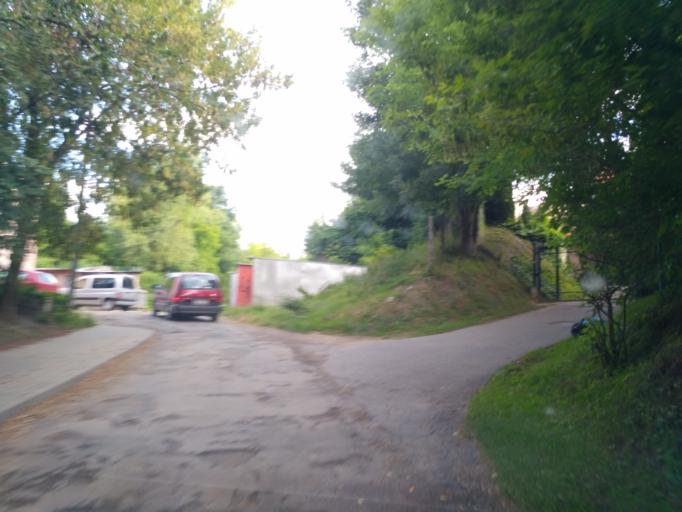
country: PL
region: Subcarpathian Voivodeship
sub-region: Przemysl
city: Przemysl
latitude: 49.7872
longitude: 22.7556
